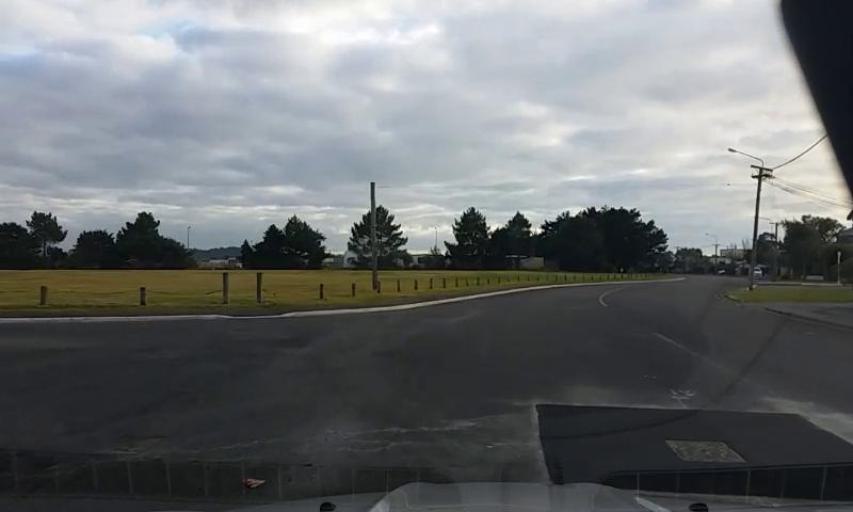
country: NZ
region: Canterbury
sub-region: Christchurch City
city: Christchurch
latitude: -43.5148
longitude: 172.7292
